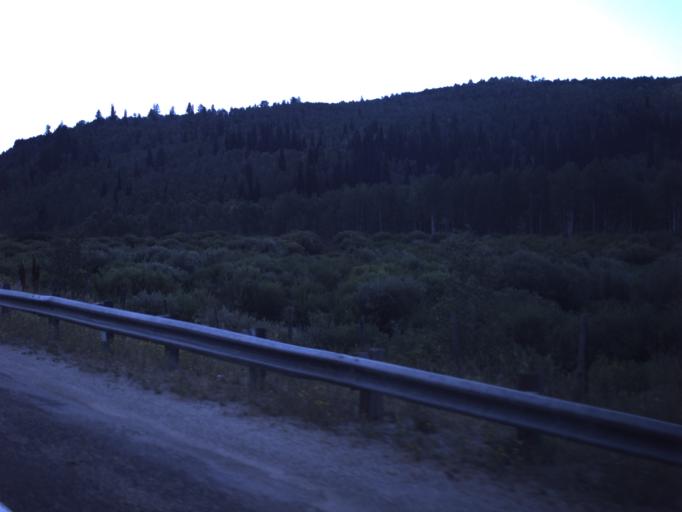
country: US
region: Utah
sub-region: Cache County
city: Richmond
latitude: 41.9093
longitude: -111.5627
